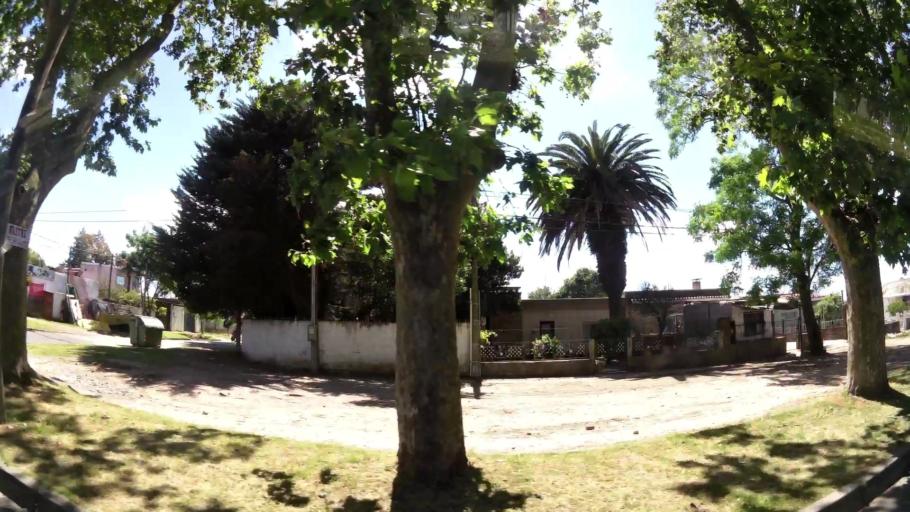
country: UY
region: Montevideo
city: Montevideo
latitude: -34.8404
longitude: -56.1376
